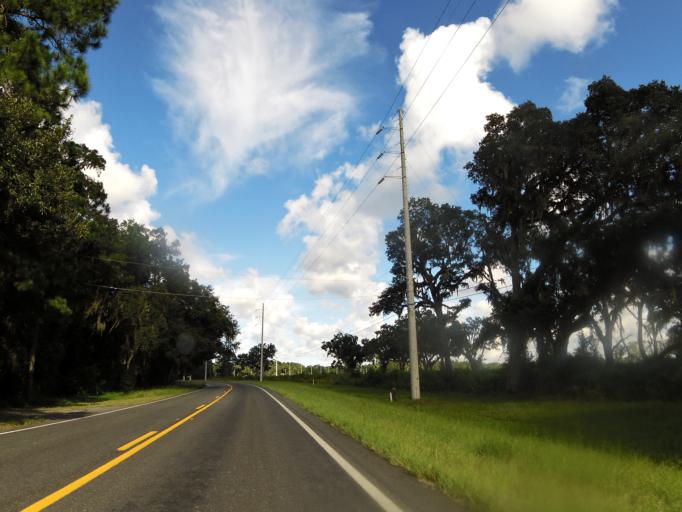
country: US
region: Georgia
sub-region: Glynn County
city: Brunswick
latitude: 31.1059
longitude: -81.6324
